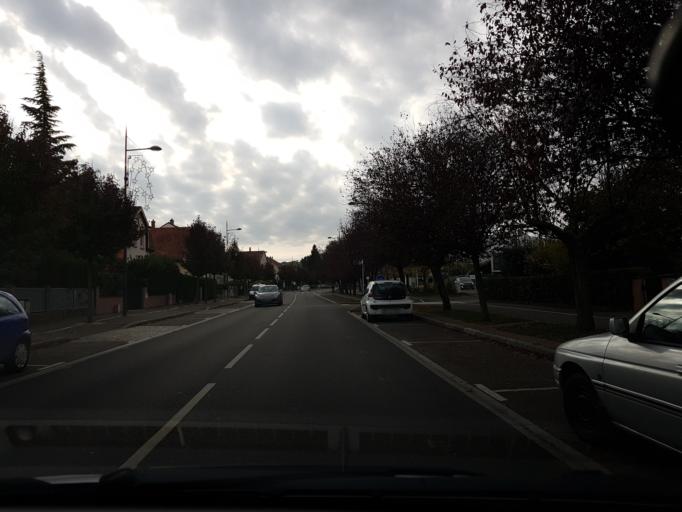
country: FR
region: Alsace
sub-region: Departement du Haut-Rhin
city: Riedisheim
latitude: 47.7456
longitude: 7.3672
